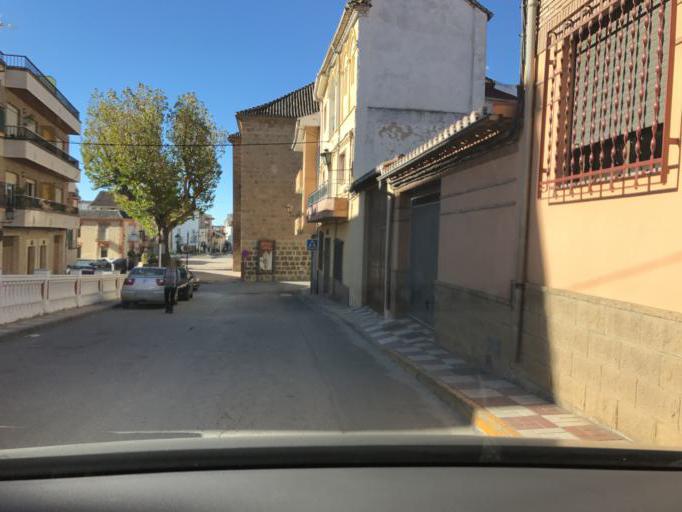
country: ES
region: Andalusia
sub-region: Provincia de Granada
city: Alfacar
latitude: 37.2371
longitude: -3.5697
